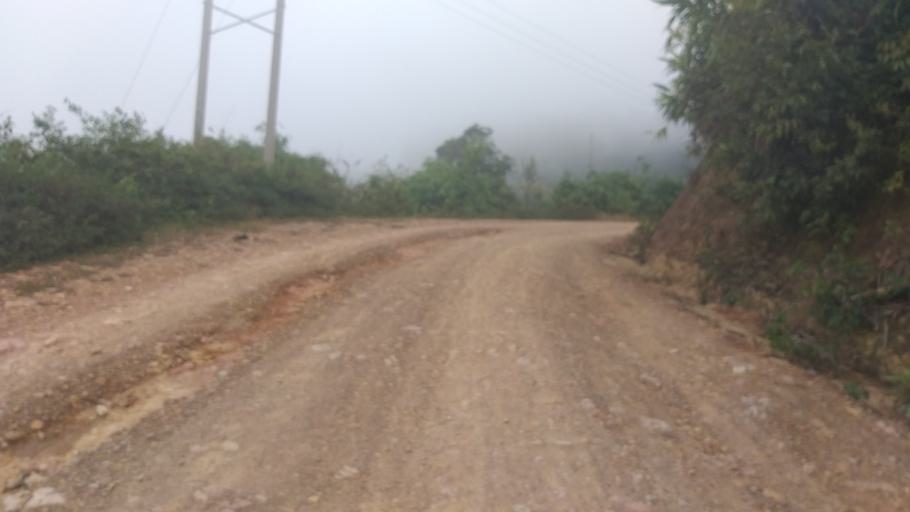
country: LA
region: Phongsali
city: Khoa
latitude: 21.2917
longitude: 102.6409
